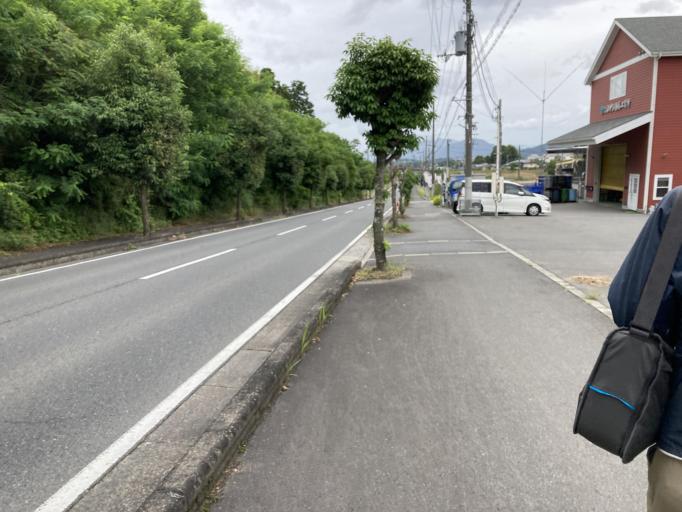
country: JP
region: Nara
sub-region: Ikoma-shi
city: Ikoma
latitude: 34.6379
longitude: 135.7069
